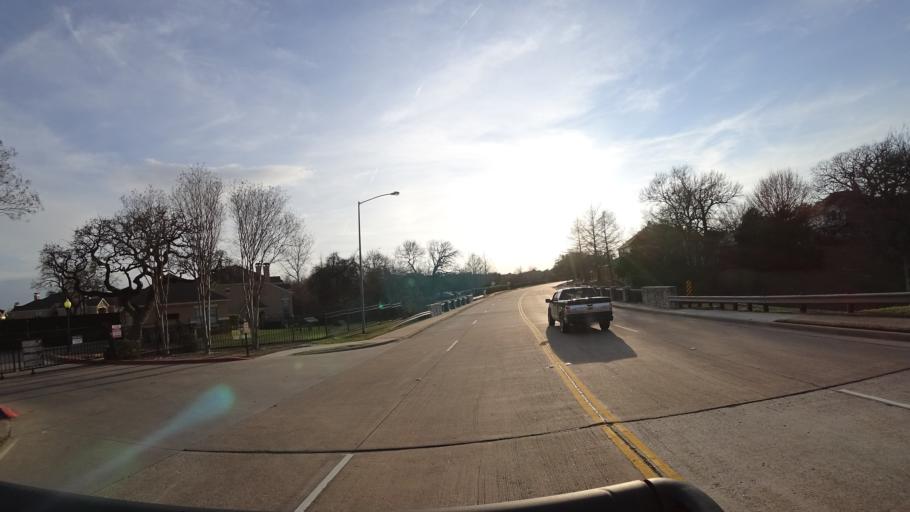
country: US
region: Texas
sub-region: Dallas County
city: Coppell
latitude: 32.9903
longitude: -96.9856
